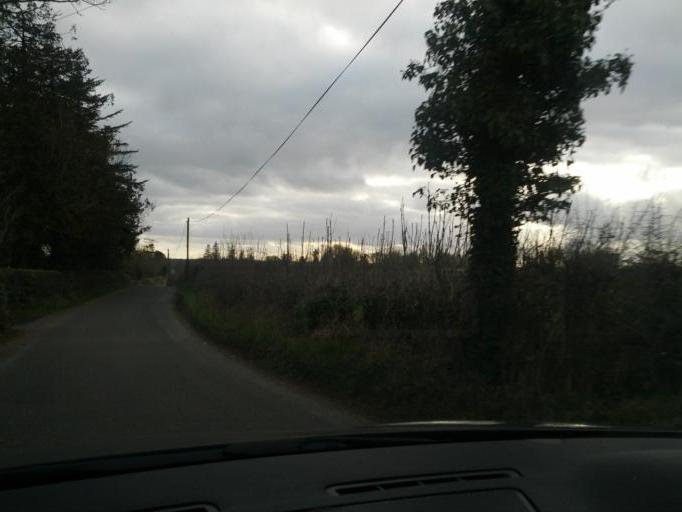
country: IE
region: Leinster
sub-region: Uibh Fhaili
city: Ferbane
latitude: 53.3786
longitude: -7.8275
